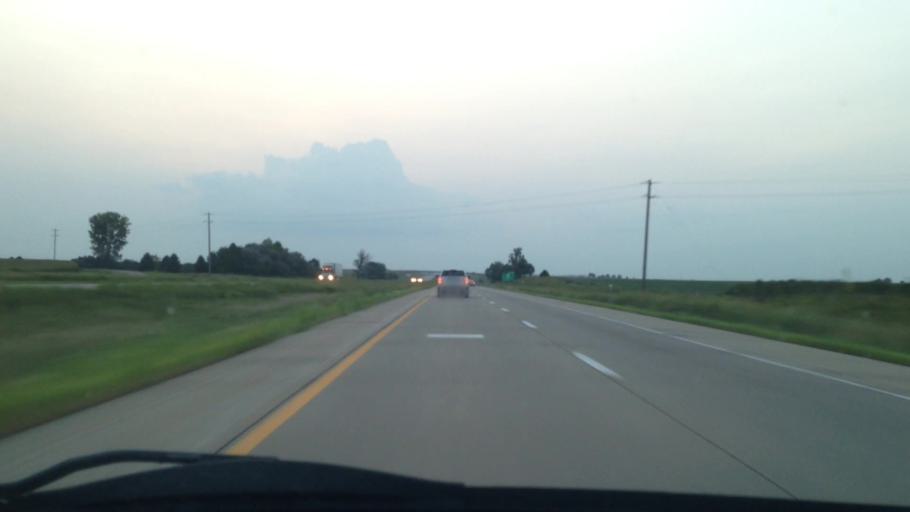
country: US
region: Iowa
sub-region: Black Hawk County
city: La Porte City
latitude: 42.3982
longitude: -92.1478
